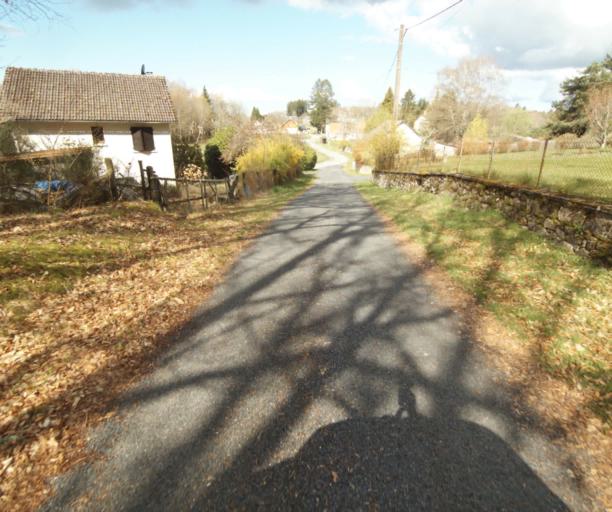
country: FR
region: Limousin
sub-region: Departement de la Correze
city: Argentat
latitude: 45.2246
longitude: 1.9351
